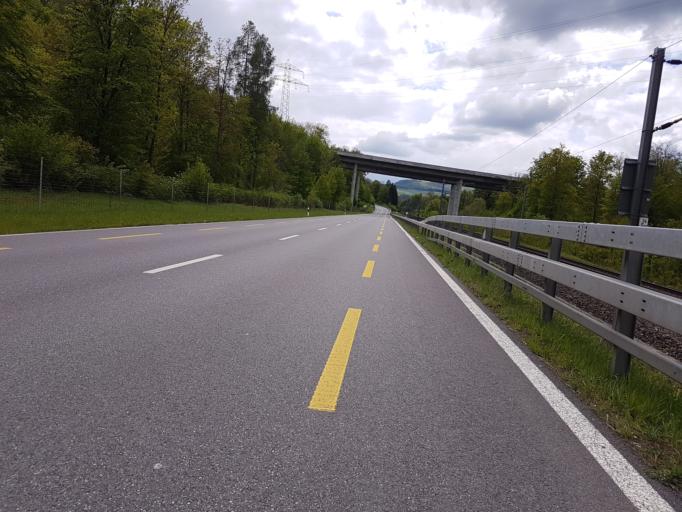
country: CH
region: Aargau
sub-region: Bezirk Brugg
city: Schinznach Bad
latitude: 47.4640
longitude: 8.1743
